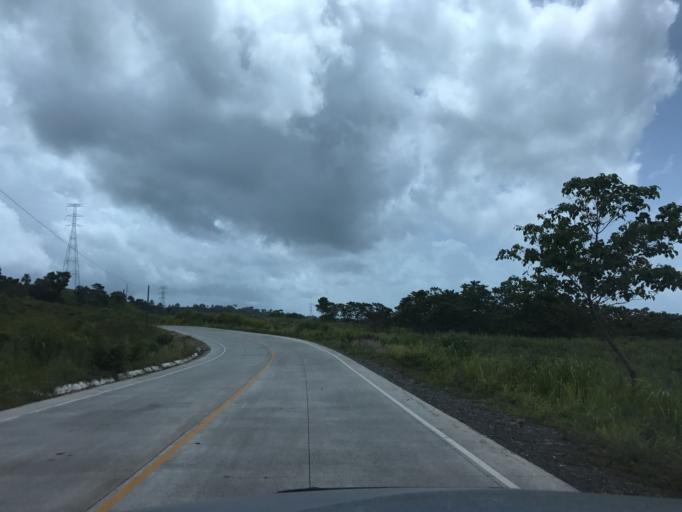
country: GT
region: Izabal
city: Morales
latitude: 15.6183
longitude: -89.0712
